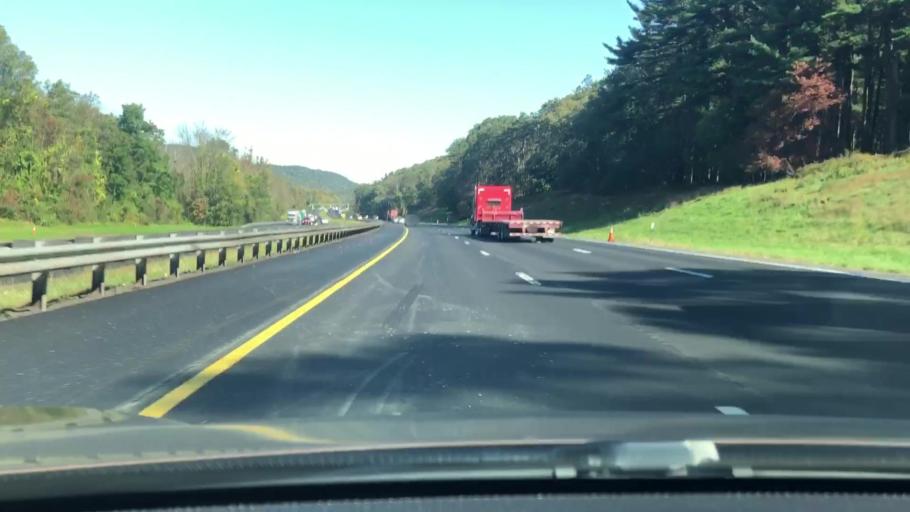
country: US
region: New York
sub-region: Orange County
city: Harriman
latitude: 41.2350
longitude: -74.1740
